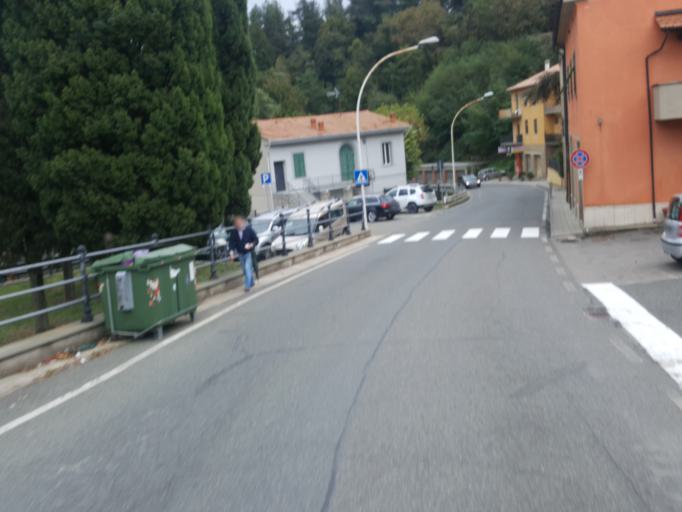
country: IT
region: Tuscany
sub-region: Province of Pisa
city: Castelnuovo di Val di Cecina
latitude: 43.2101
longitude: 10.9029
